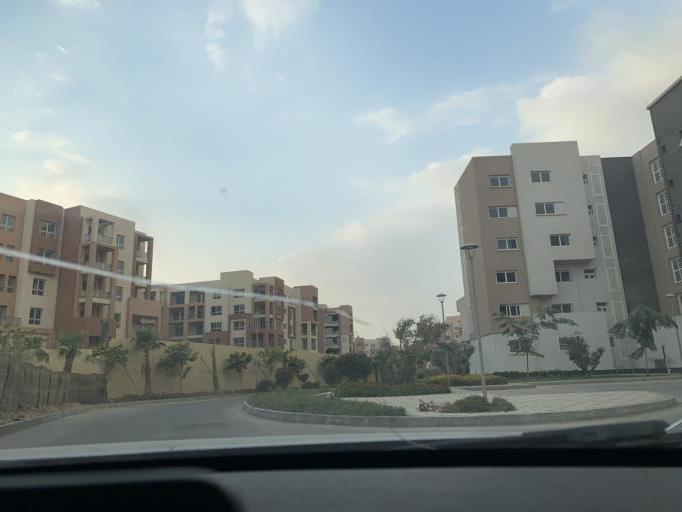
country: EG
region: Muhafazat al Qalyubiyah
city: Al Khankah
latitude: 30.1013
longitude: 31.6511
